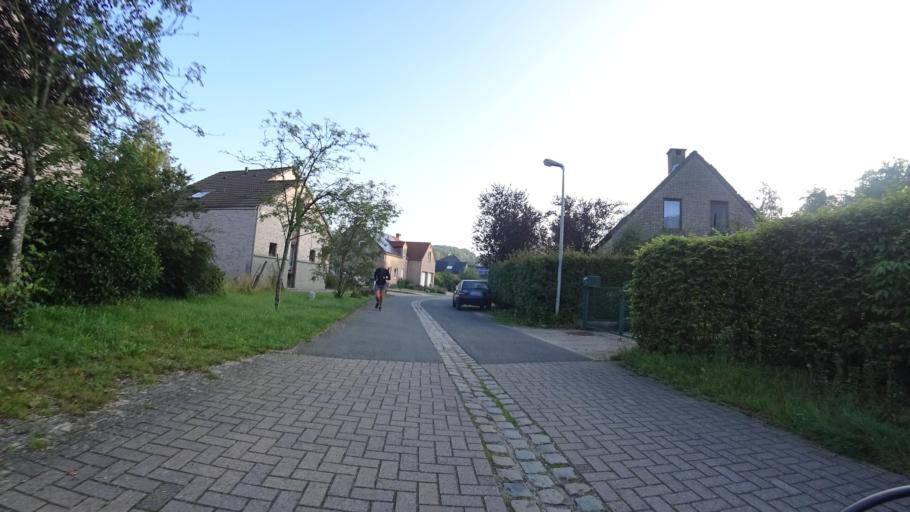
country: BE
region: Wallonia
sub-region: Province du Brabant Wallon
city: Mont-Saint-Guibert
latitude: 50.6371
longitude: 4.6231
